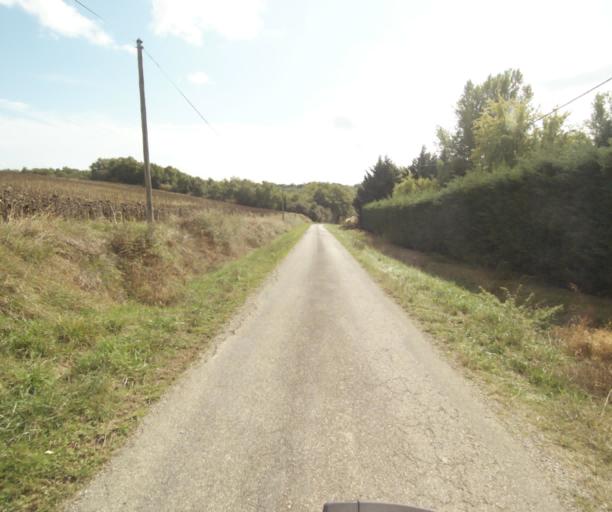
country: FR
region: Midi-Pyrenees
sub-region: Departement du Tarn-et-Garonne
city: Verdun-sur-Garonne
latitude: 43.8585
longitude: 1.1779
